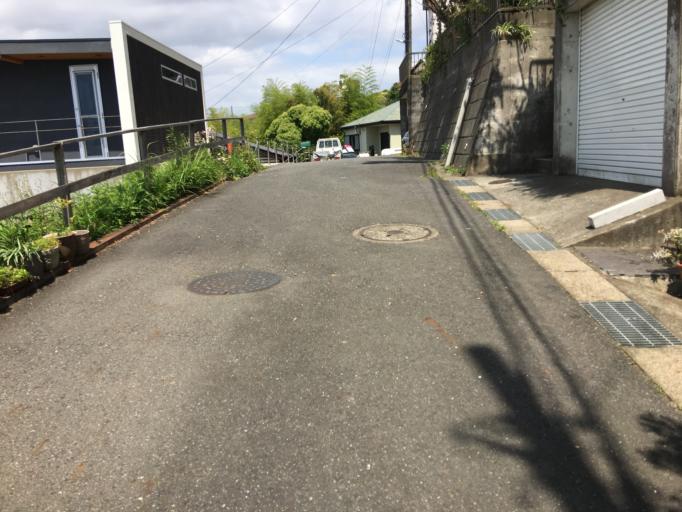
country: JP
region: Kanagawa
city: Kamakura
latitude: 35.3439
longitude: 139.5452
